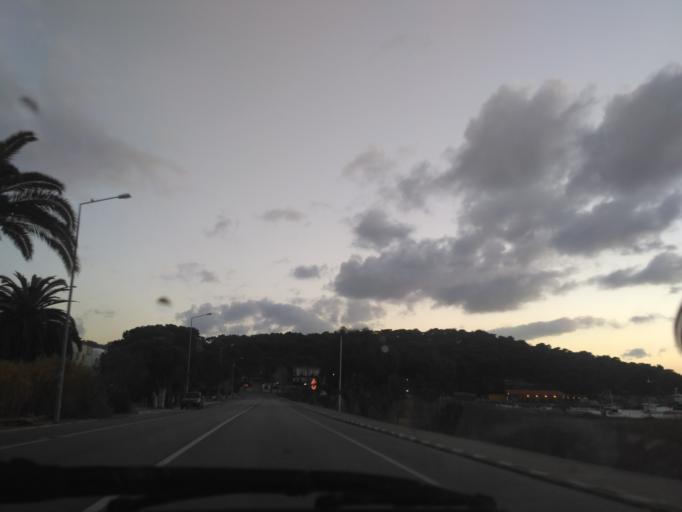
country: TR
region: Balikesir
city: Ayvalik
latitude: 39.3019
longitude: 26.6638
